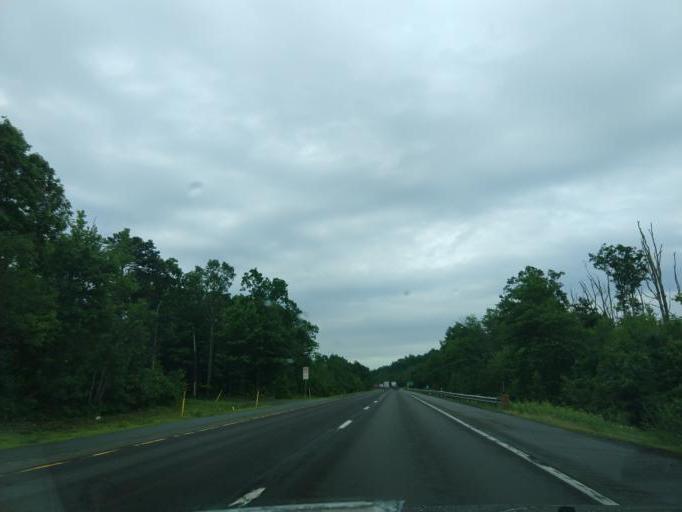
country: US
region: Pennsylvania
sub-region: Luzerne County
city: West Hazleton
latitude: 40.9515
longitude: -76.0275
